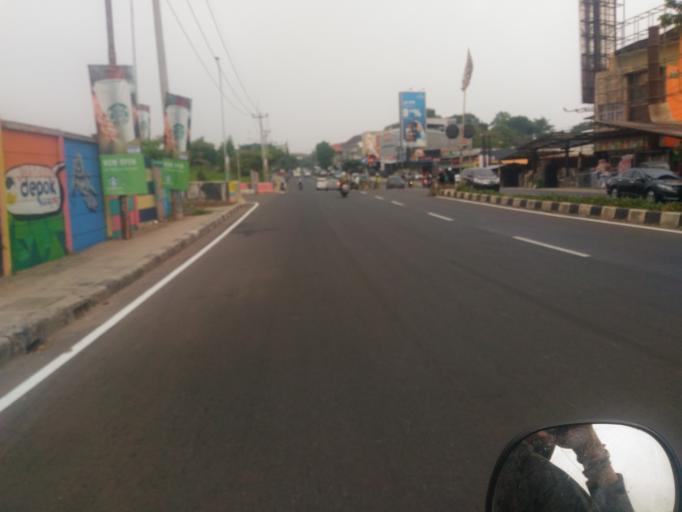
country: ID
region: West Java
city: Depok
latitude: -6.3786
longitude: 106.8363
